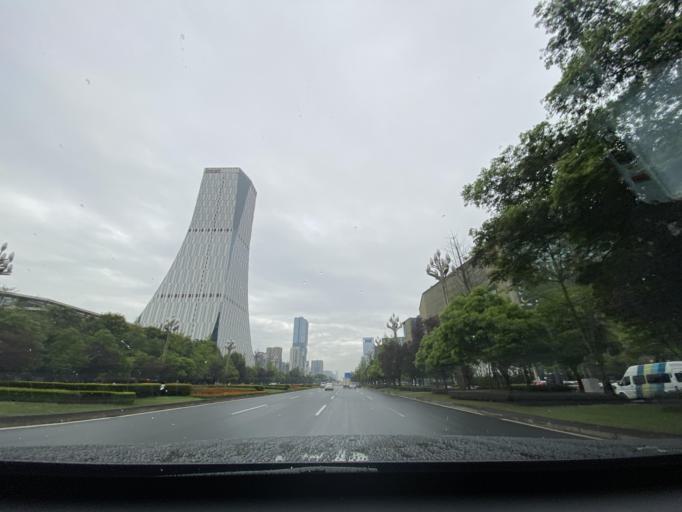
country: CN
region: Sichuan
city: Chengdu
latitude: 30.5415
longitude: 104.0668
